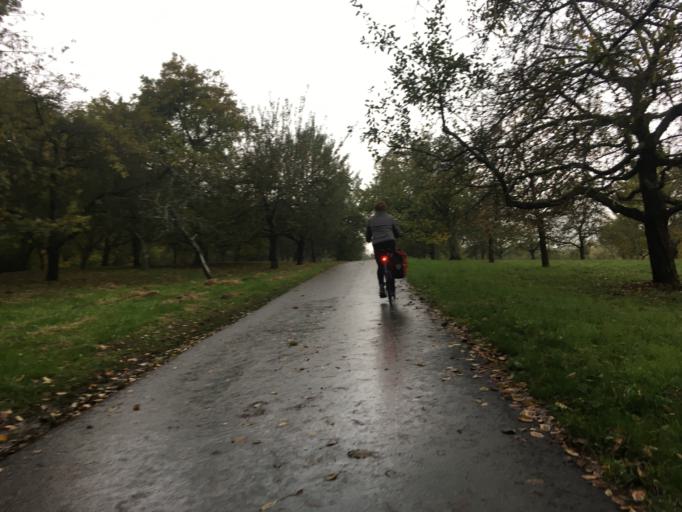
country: DE
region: Baden-Wuerttemberg
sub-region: Tuebingen Region
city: Nehren
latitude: 48.4210
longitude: 9.0799
